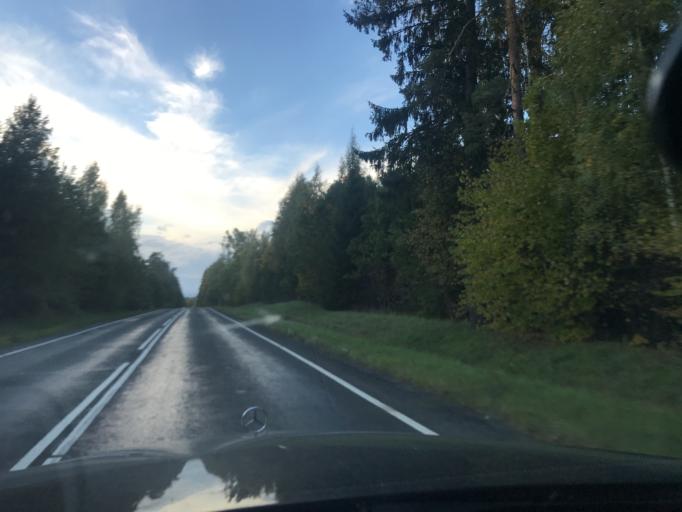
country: EE
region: Vorumaa
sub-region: Antsla vald
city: Vana-Antsla
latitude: 57.8741
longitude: 26.5897
